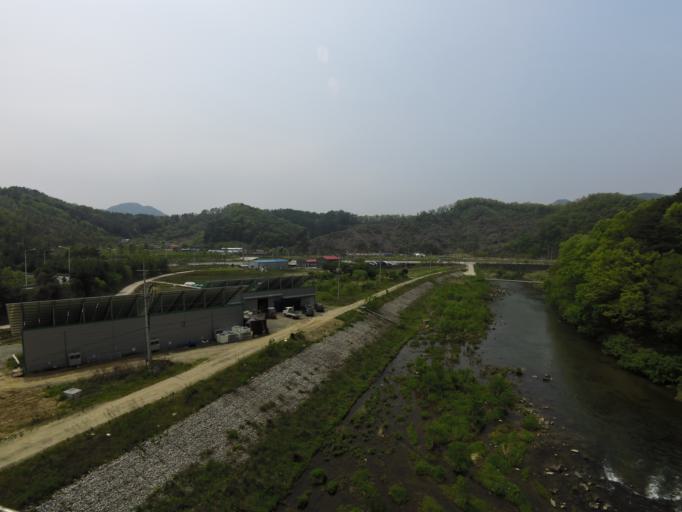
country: KR
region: Chungcheongbuk-do
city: Okcheon
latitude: 36.3194
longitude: 127.5494
